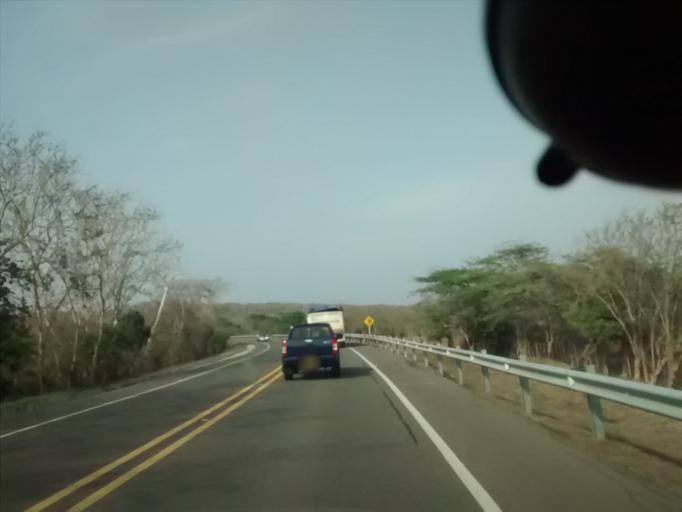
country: CO
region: Atlantico
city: Juan de Acosta
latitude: 10.8463
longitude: -75.1317
